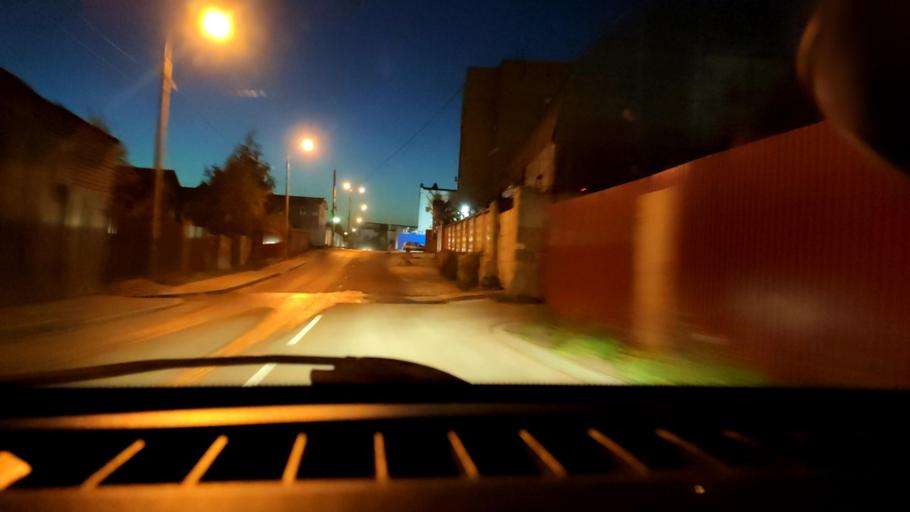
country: RU
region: Samara
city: Samara
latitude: 53.1787
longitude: 50.1437
